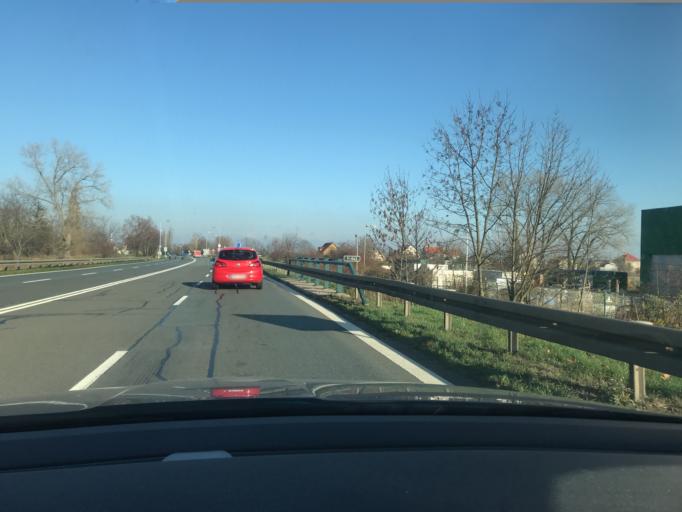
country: CZ
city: Stezery
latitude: 50.2193
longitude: 15.7886
